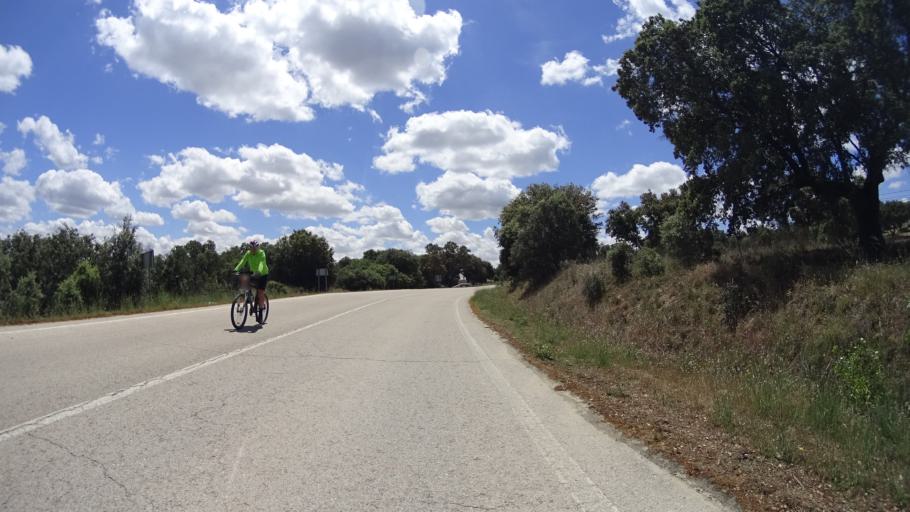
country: ES
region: Madrid
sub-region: Provincia de Madrid
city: Villanueva del Pardillo
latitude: 40.4510
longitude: -3.9533
